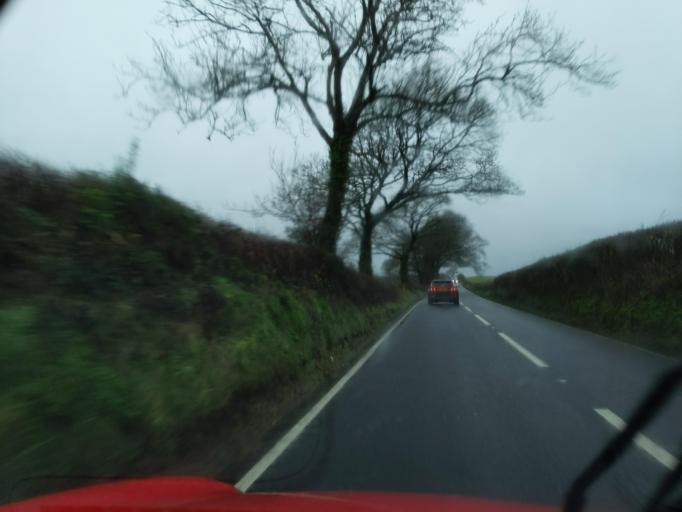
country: GB
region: England
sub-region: Cornwall
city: Launceston
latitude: 50.6185
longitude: -4.3396
